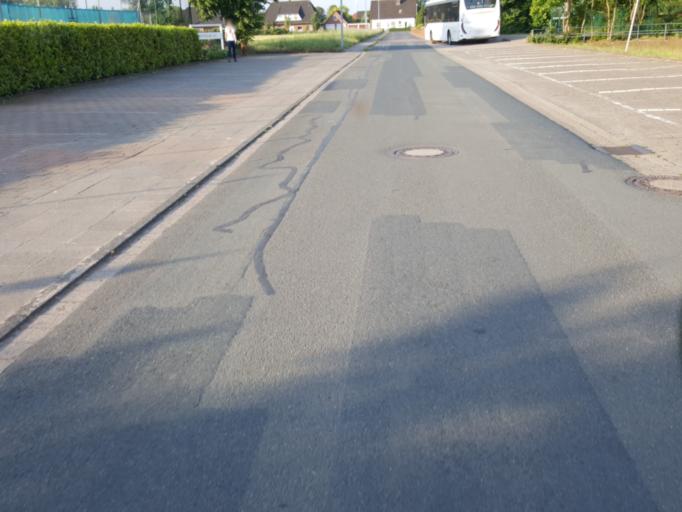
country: DE
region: Lower Saxony
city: Landesbergen
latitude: 52.5589
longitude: 9.1254
